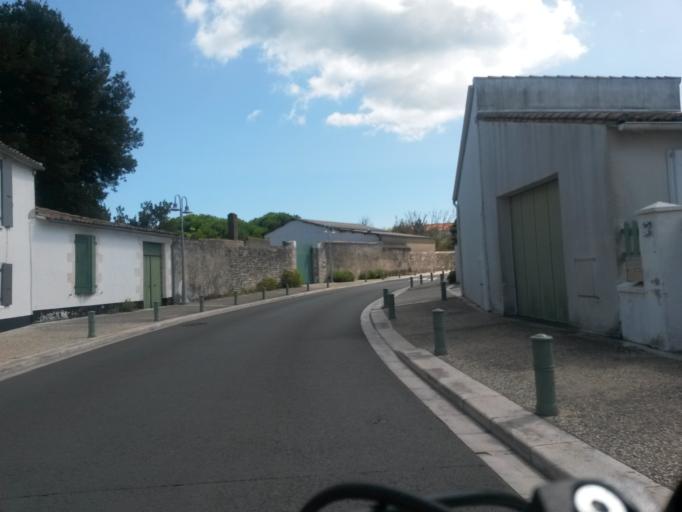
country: FR
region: Poitou-Charentes
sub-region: Departement de la Charente-Maritime
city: La Flotte
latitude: 46.1863
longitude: -1.3200
